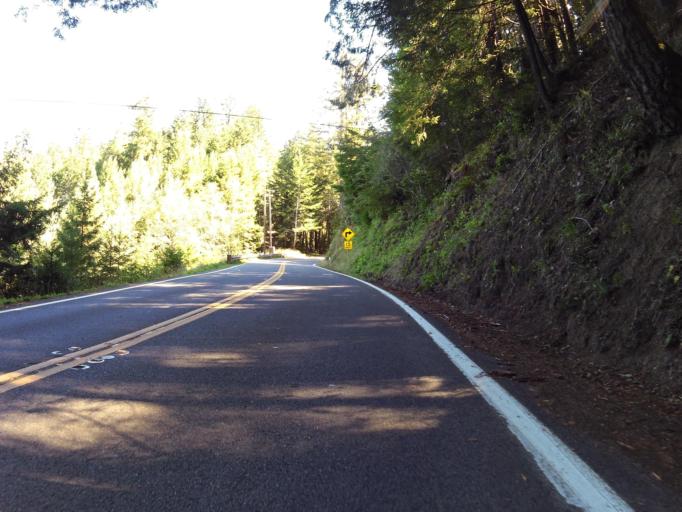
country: US
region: California
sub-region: Mendocino County
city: Fort Bragg
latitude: 39.7251
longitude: -123.8099
